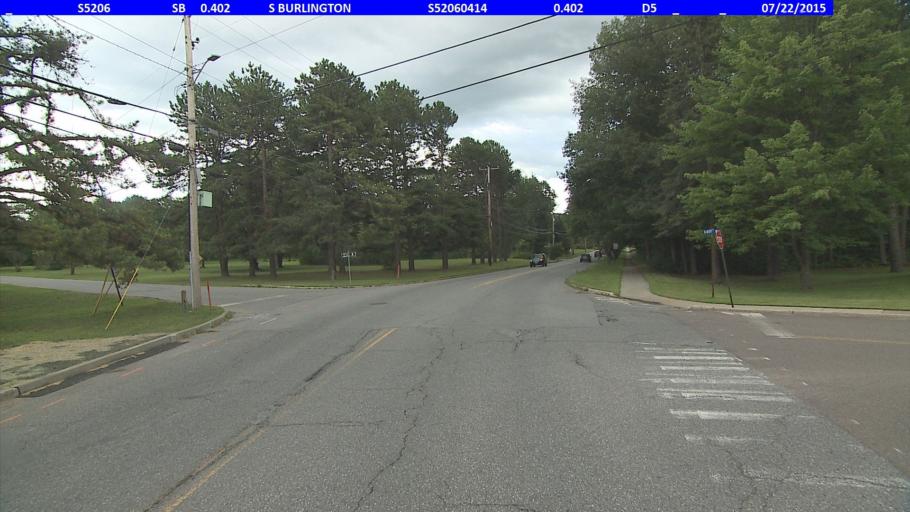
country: US
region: Vermont
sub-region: Chittenden County
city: South Burlington
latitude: 44.4762
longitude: -73.1658
